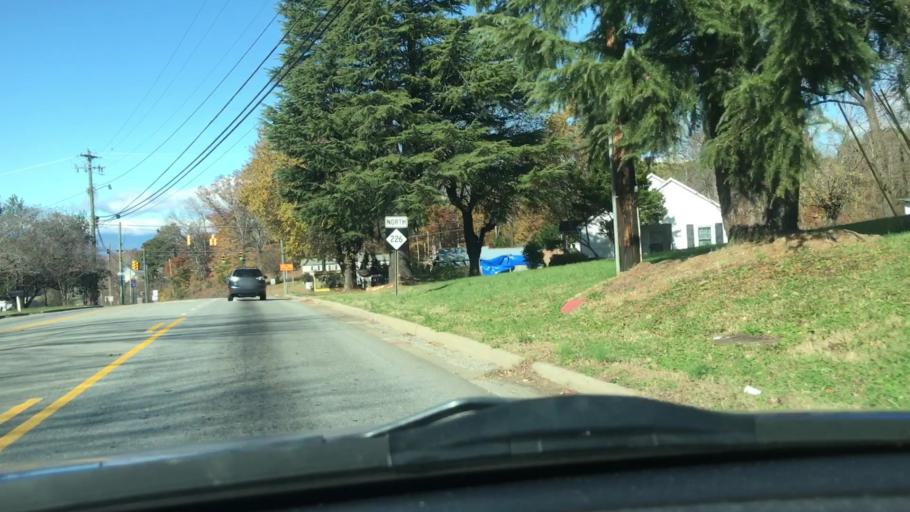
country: US
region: North Carolina
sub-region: McDowell County
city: Marion
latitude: 35.6598
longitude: -81.9648
